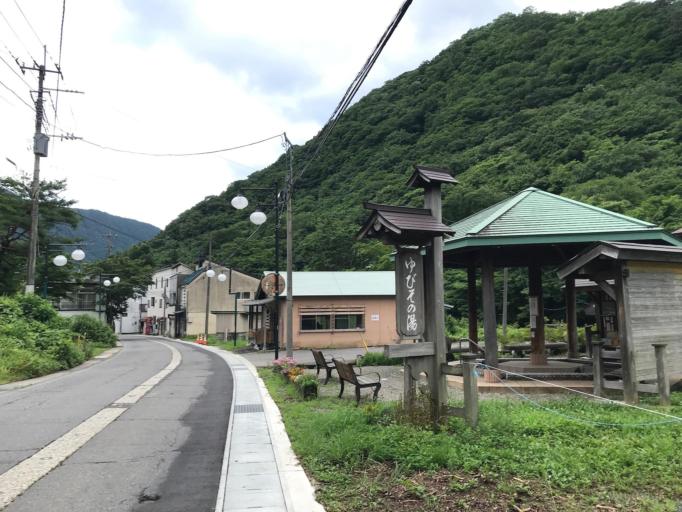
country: JP
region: Gunma
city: Numata
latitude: 36.8073
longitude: 138.9864
